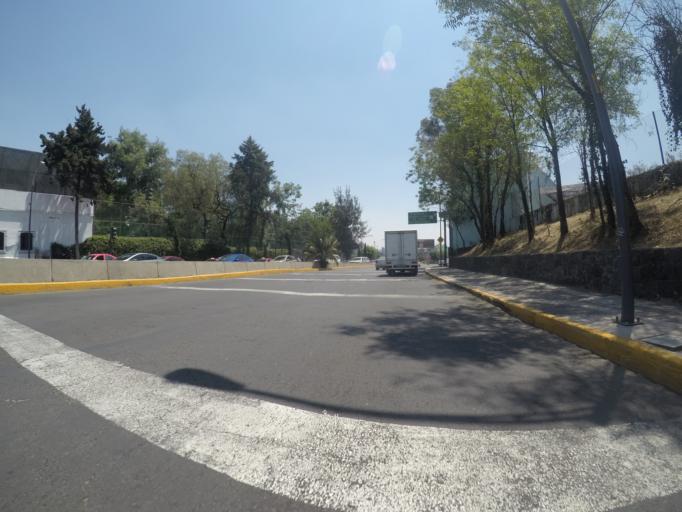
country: MX
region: Mexico City
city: Polanco
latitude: 19.4130
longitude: -99.1921
